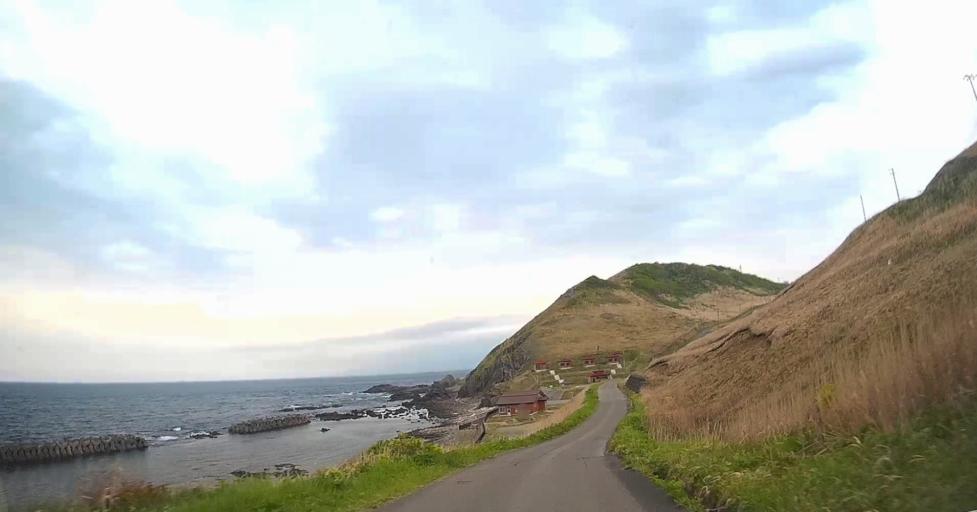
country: JP
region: Aomori
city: Shimokizukuri
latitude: 41.2510
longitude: 140.3435
